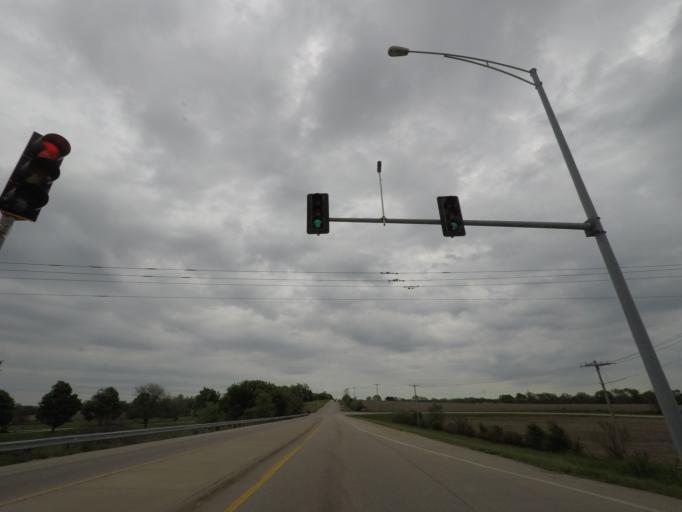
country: US
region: Illinois
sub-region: Winnebago County
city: Roscoe
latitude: 42.4569
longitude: -88.9934
